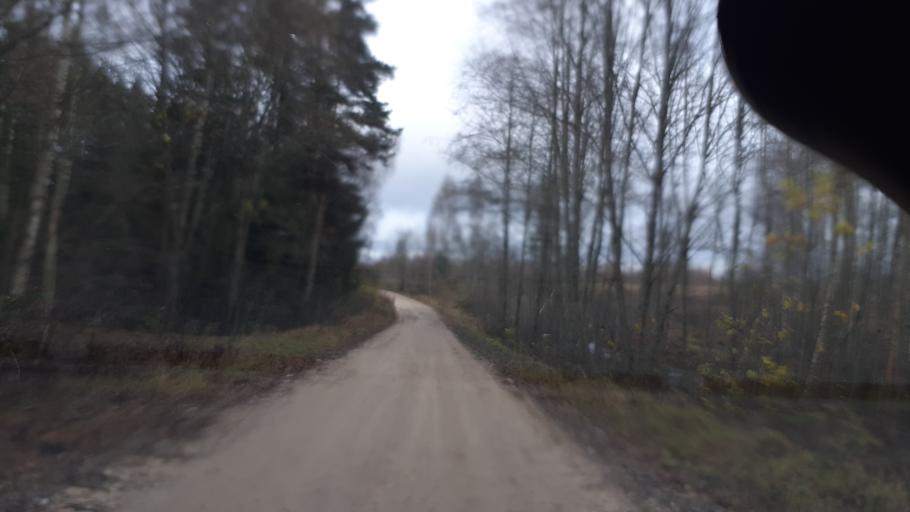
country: LV
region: Kuldigas Rajons
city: Kuldiga
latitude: 57.0369
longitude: 21.8800
